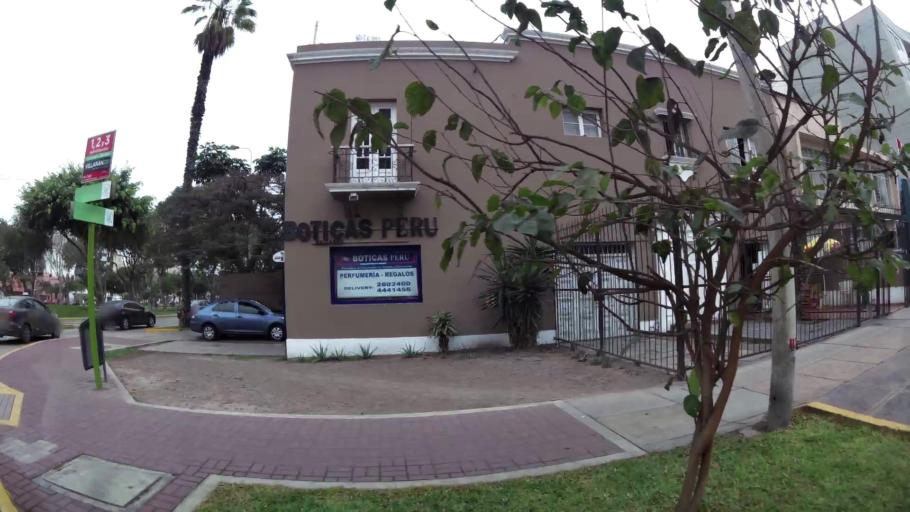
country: PE
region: Lima
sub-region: Lima
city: Surco
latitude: -12.1218
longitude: -77.0202
